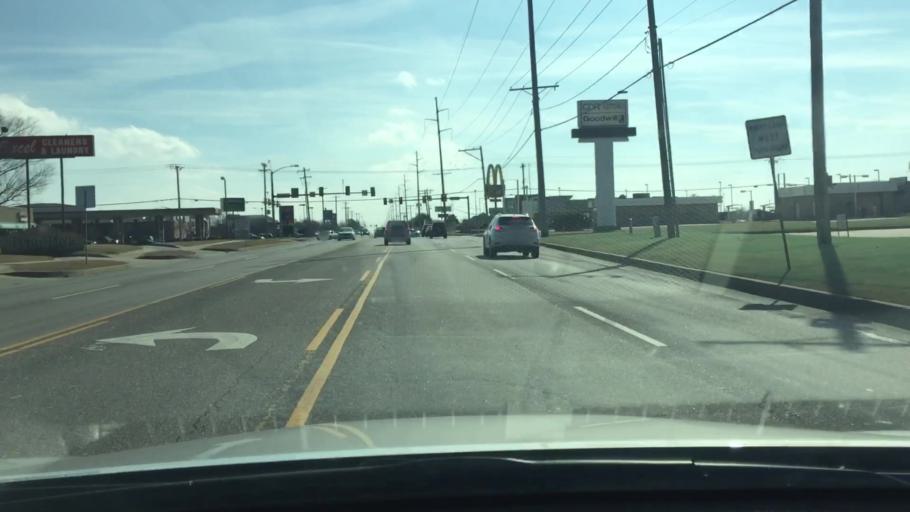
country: US
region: Oklahoma
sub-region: Cleveland County
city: Moore
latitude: 35.3785
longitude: -97.5479
